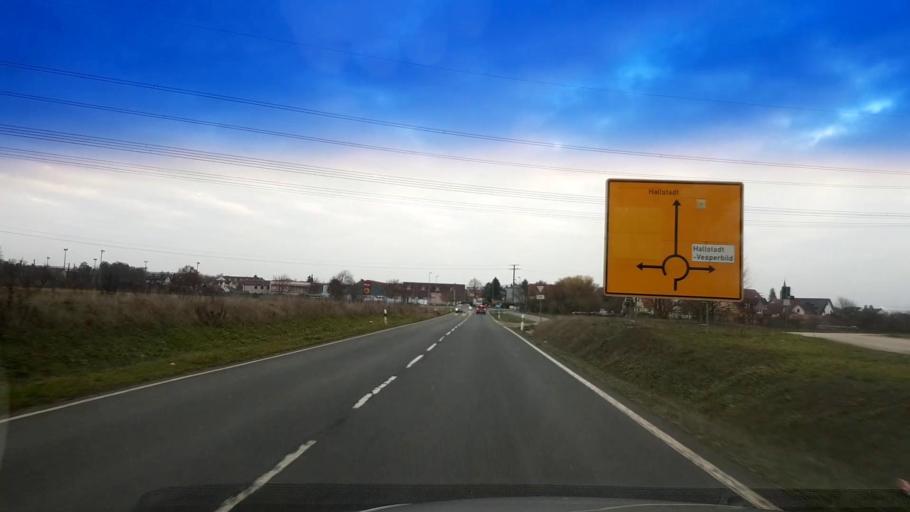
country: DE
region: Bavaria
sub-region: Upper Franconia
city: Hallstadt
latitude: 49.9364
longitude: 10.8824
